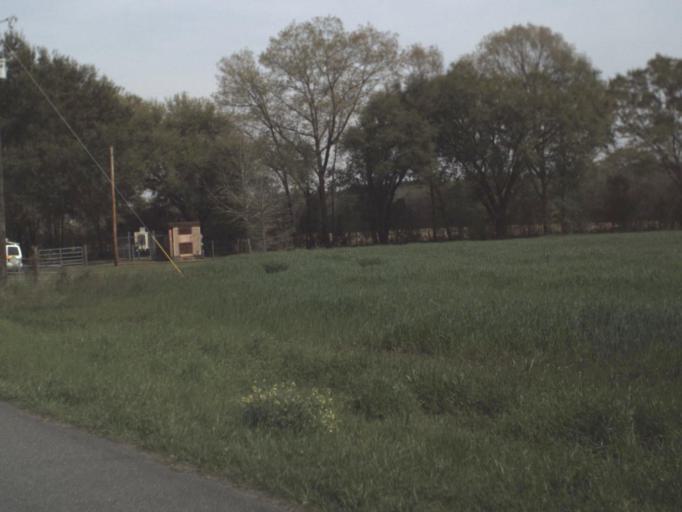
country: US
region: Florida
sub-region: Jackson County
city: Malone
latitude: 30.9643
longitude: -85.1147
